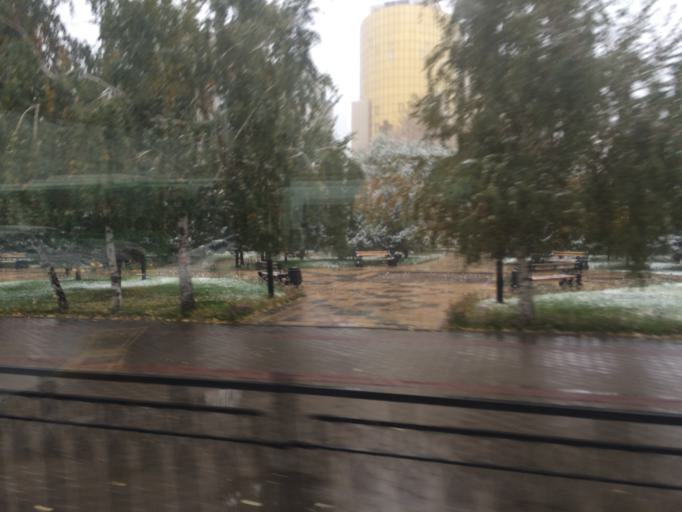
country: KZ
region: Astana Qalasy
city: Astana
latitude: 51.1650
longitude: 71.4273
